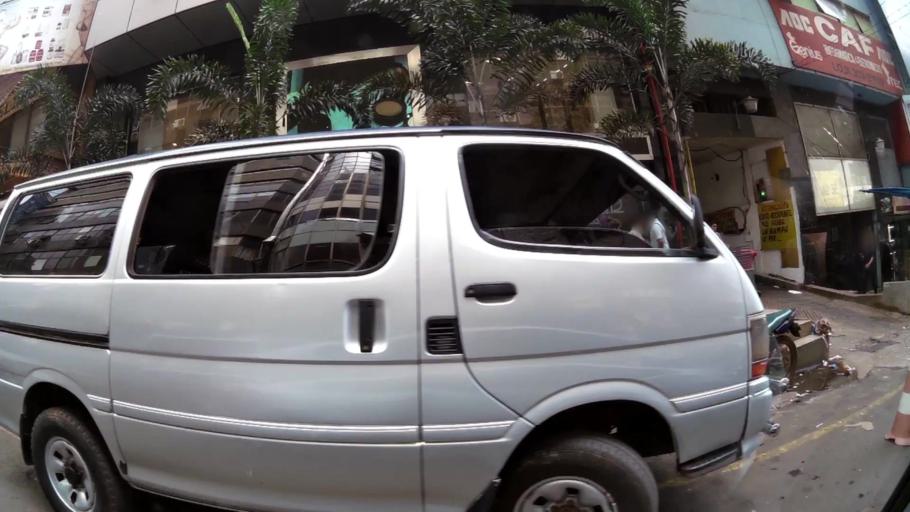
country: PY
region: Alto Parana
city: Ciudad del Este
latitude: -25.5110
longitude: -54.6082
